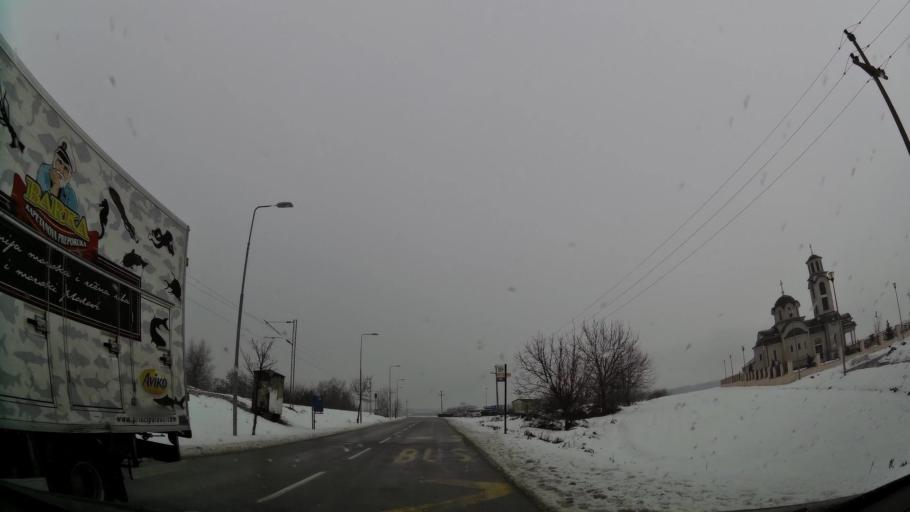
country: RS
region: Central Serbia
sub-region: Belgrade
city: Zemun
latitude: 44.8447
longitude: 20.3489
